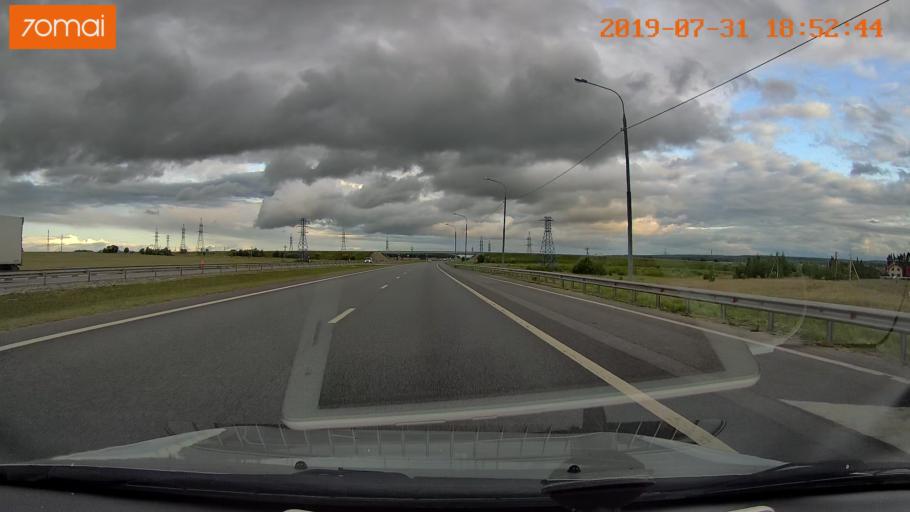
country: RU
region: Moskovskaya
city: Voskresensk
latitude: 55.2108
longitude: 38.6384
